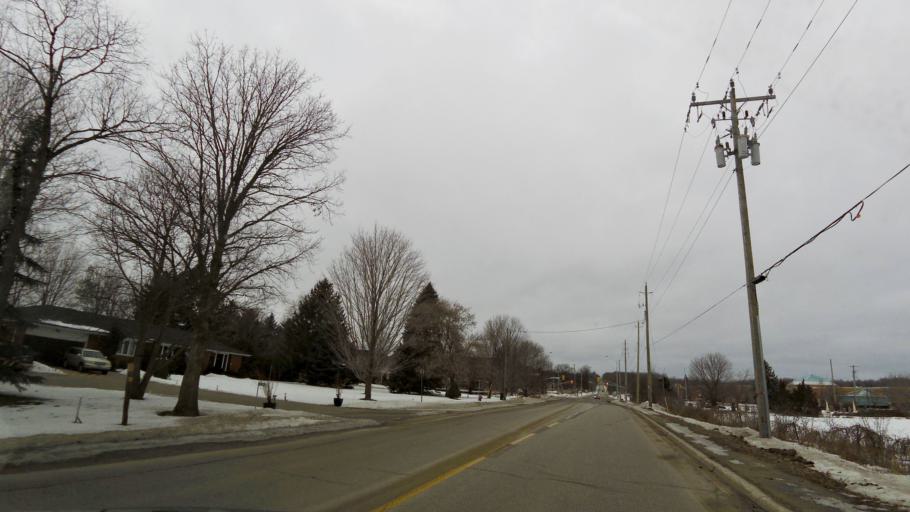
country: CA
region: Ontario
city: Brampton
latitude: 43.8777
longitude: -79.8536
